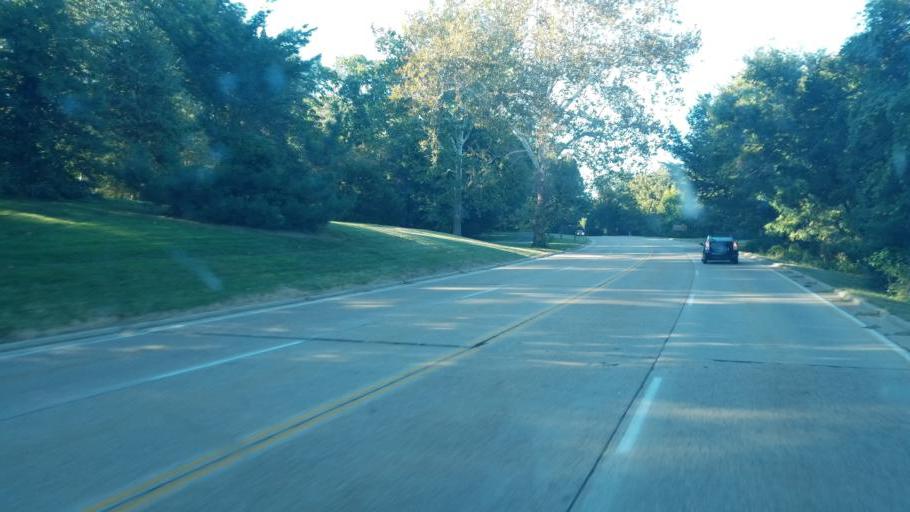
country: US
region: Virginia
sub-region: Fairfax County
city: Fort Hunt
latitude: 38.7268
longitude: -77.0419
